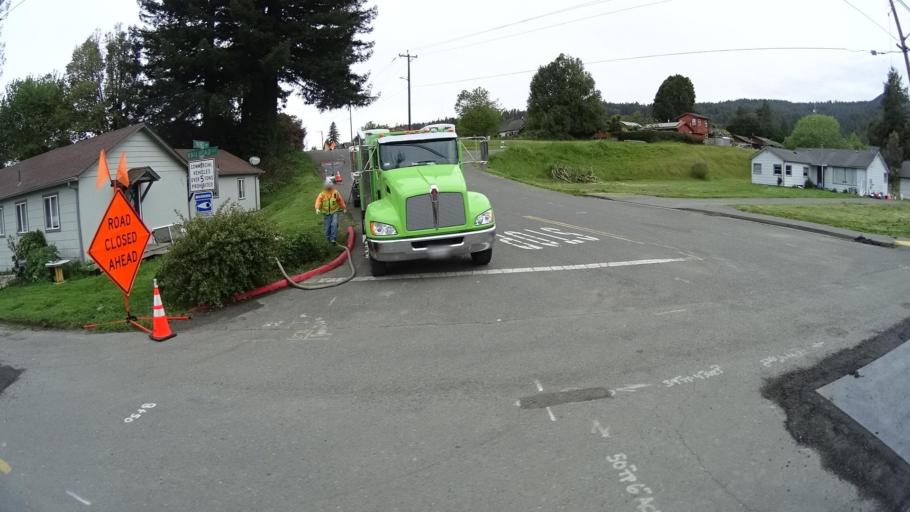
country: US
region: California
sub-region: Humboldt County
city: Blue Lake
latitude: 40.8798
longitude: -123.9844
